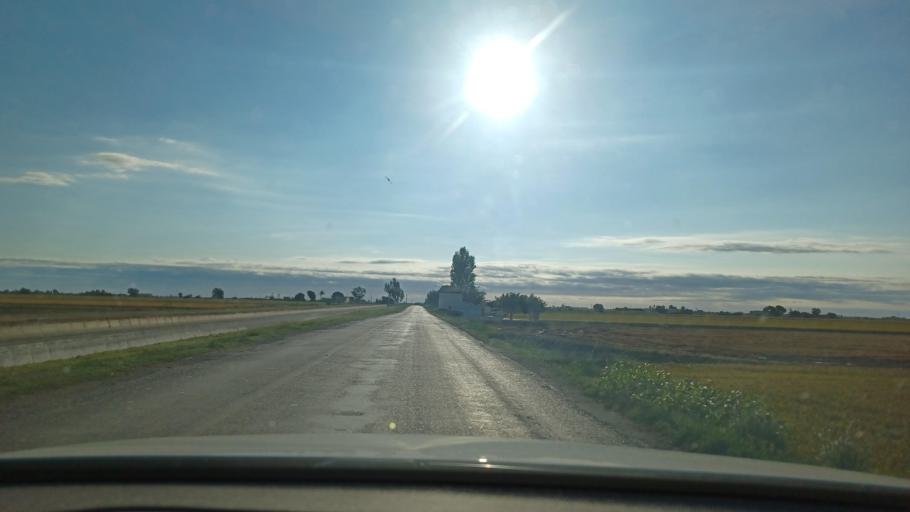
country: ES
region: Catalonia
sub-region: Provincia de Tarragona
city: Amposta
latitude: 40.6998
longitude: 0.6085
